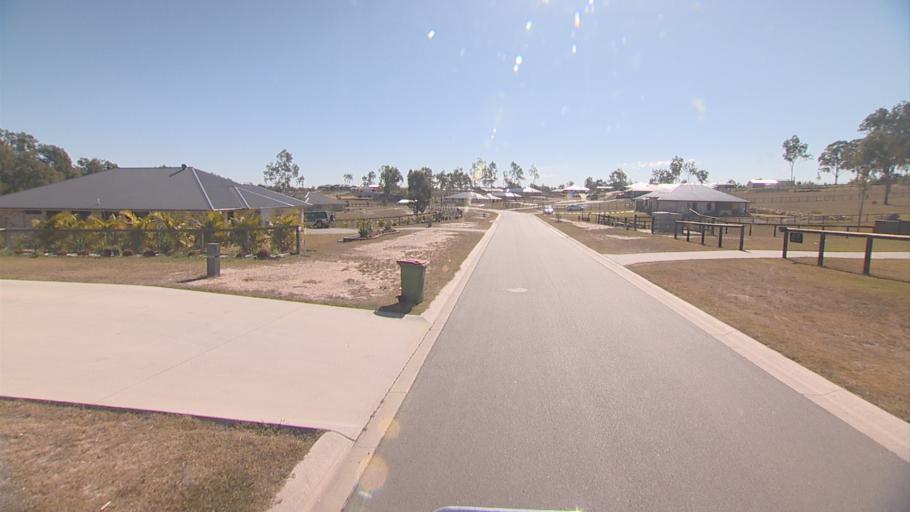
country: AU
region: Queensland
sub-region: Logan
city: Cedar Vale
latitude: -27.8666
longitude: 153.0455
